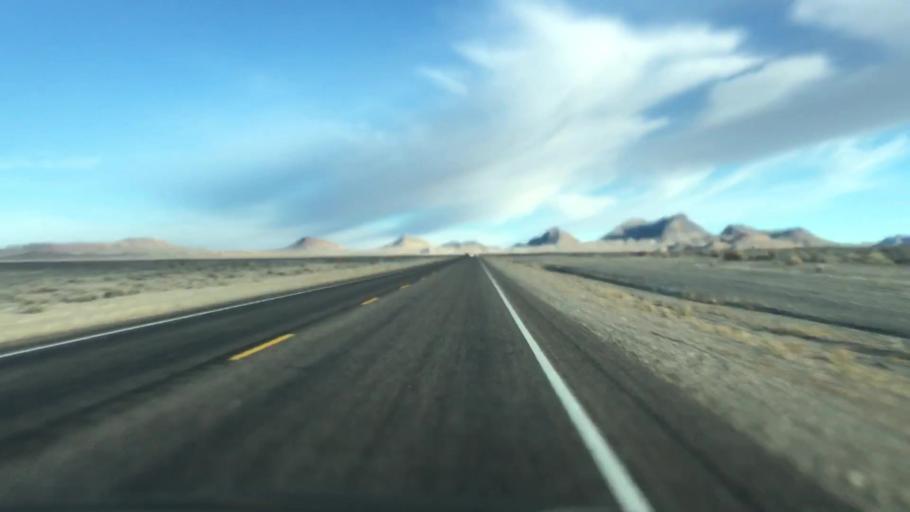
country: US
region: Nevada
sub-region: Nye County
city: Tonopah
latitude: 38.0959
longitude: -117.3156
